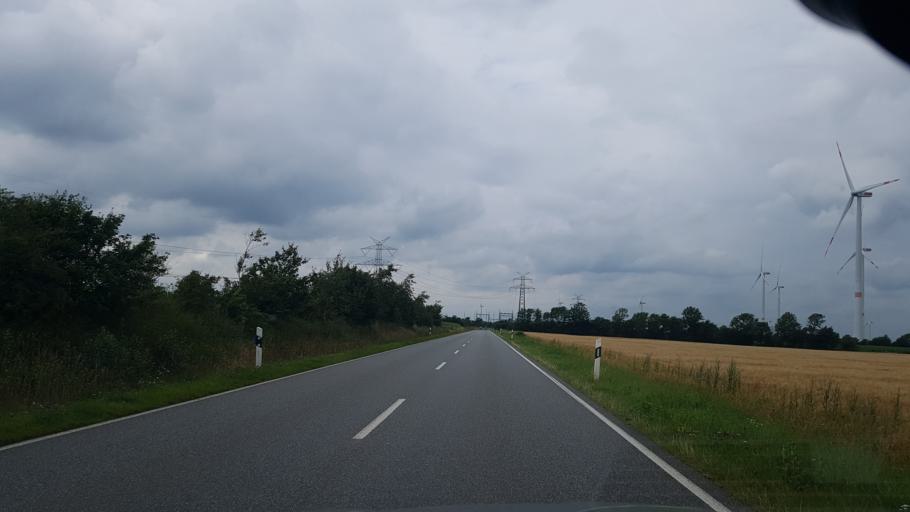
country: DE
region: Schleswig-Holstein
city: Jardelund
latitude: 54.8438
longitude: 9.2069
